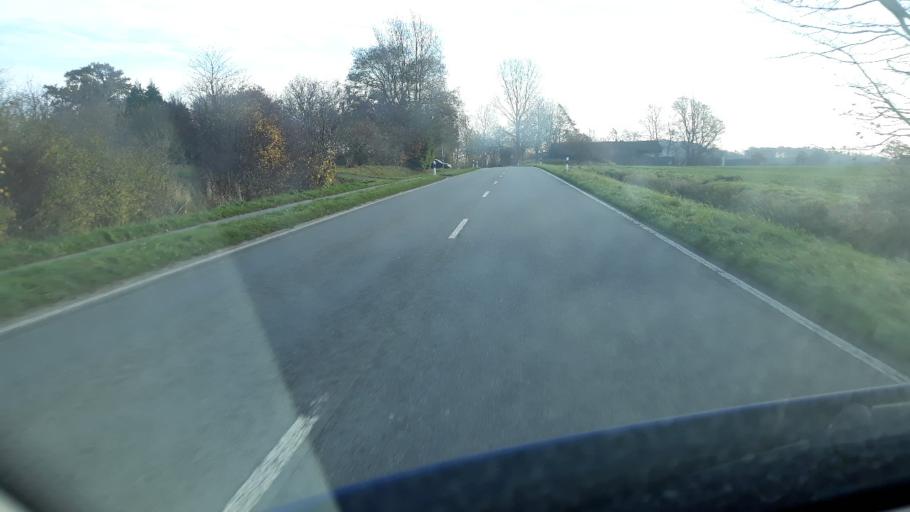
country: DE
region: Schleswig-Holstein
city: Kappeln
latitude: 54.6628
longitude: 9.9596
